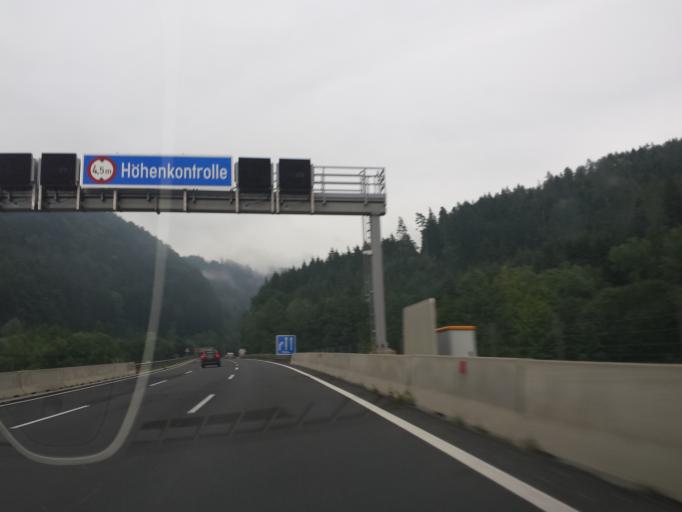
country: AT
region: Styria
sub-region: Politischer Bezirk Bruck-Muerzzuschlag
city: Bruck an der Mur
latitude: 47.4212
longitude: 15.2969
